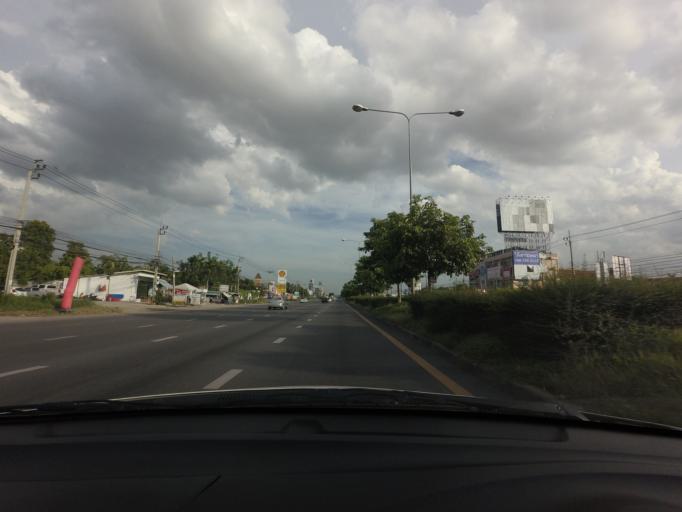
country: TH
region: Nonthaburi
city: Bang Bua Thong
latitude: 13.8936
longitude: 100.4502
